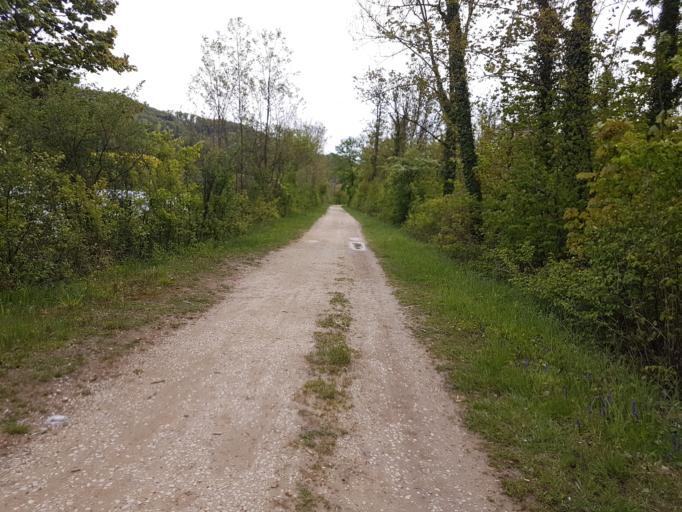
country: CH
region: Aargau
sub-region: Bezirk Brugg
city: Schinznach Bad
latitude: 47.4437
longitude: 8.1639
